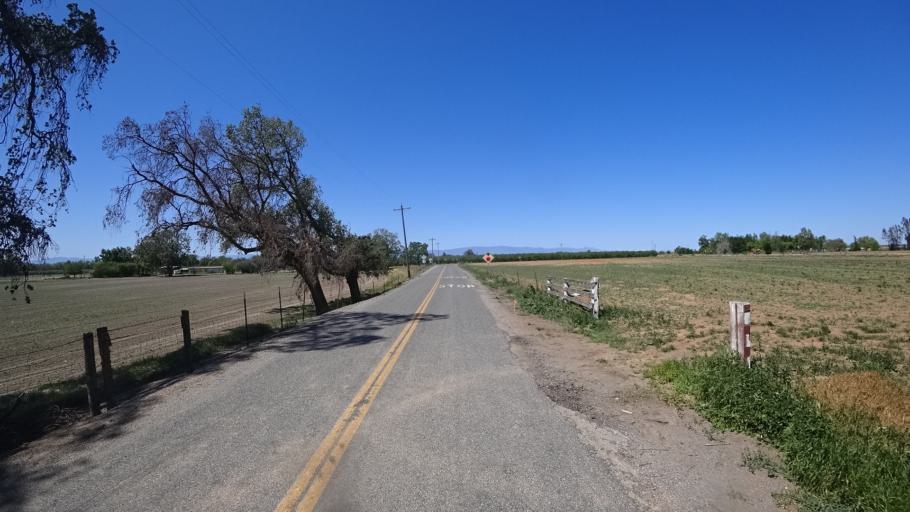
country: US
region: California
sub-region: Glenn County
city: Orland
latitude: 39.7918
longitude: -122.2278
